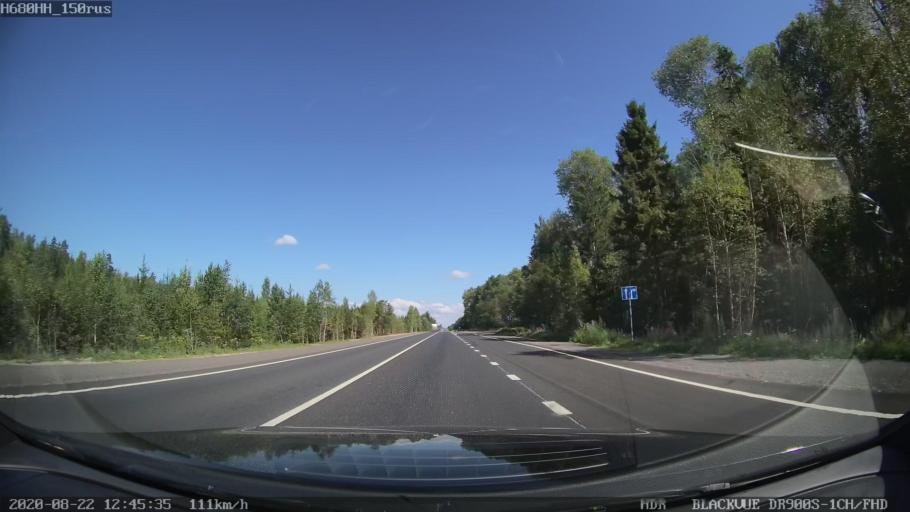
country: RU
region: Tverskaya
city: Rameshki
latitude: 57.4073
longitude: 36.1249
